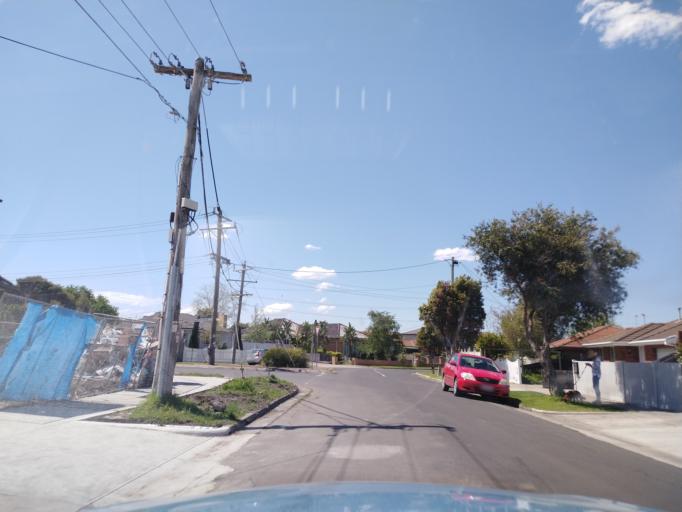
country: AU
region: Victoria
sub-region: Hobsons Bay
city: South Kingsville
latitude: -37.8387
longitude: 144.8621
